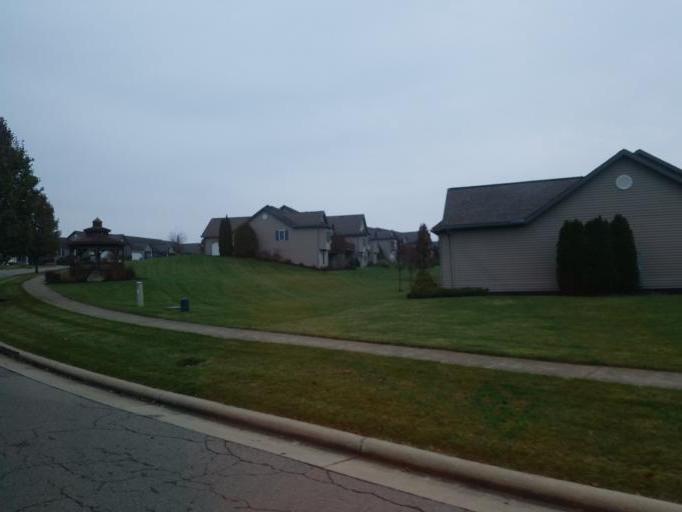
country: US
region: Ohio
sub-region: Richland County
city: Mansfield
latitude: 40.7128
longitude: -82.5241
